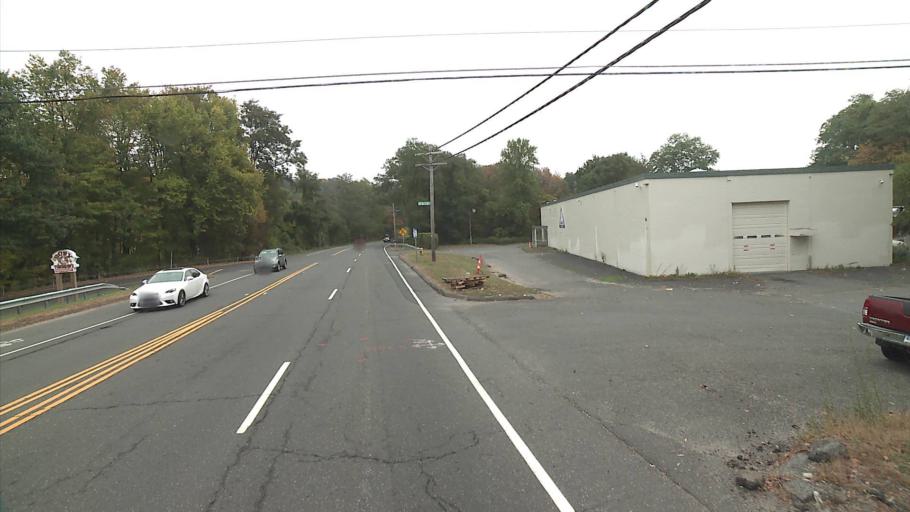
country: US
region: Connecticut
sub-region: Fairfield County
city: Danbury
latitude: 41.3936
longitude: -73.5168
